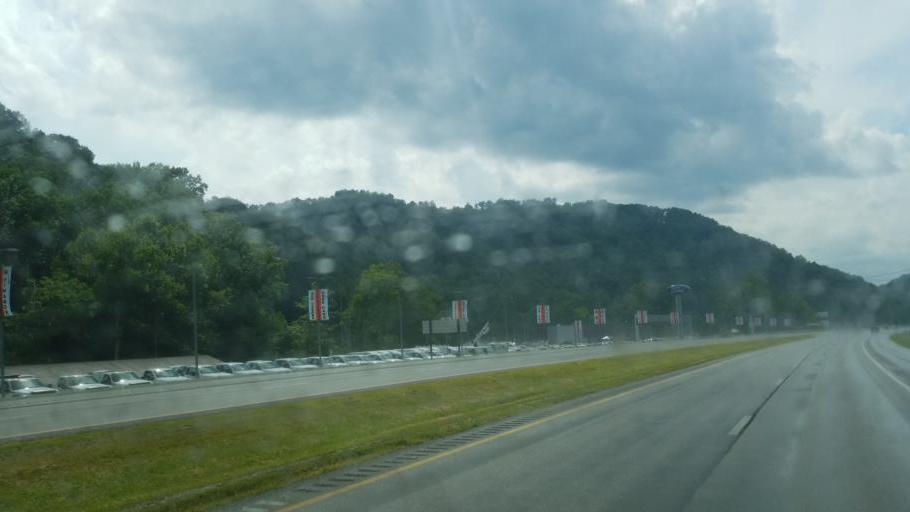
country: US
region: West Virginia
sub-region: Logan County
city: Chapmanville
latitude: 37.9876
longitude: -81.9682
